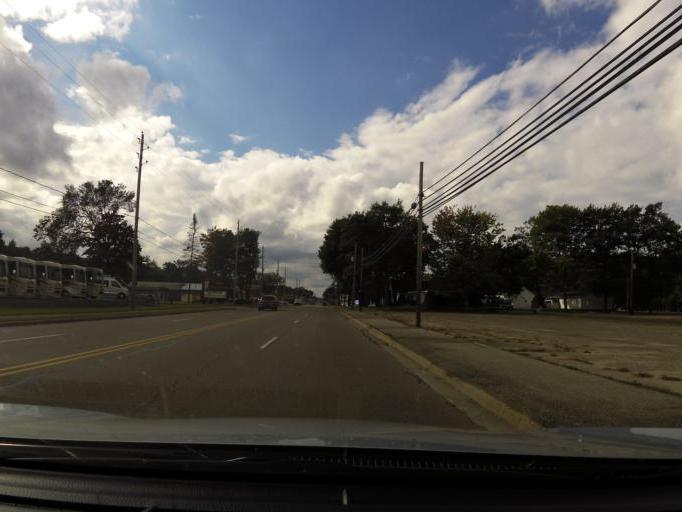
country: US
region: Michigan
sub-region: Roscommon County
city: Prudenville
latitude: 44.2987
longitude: -84.6941
